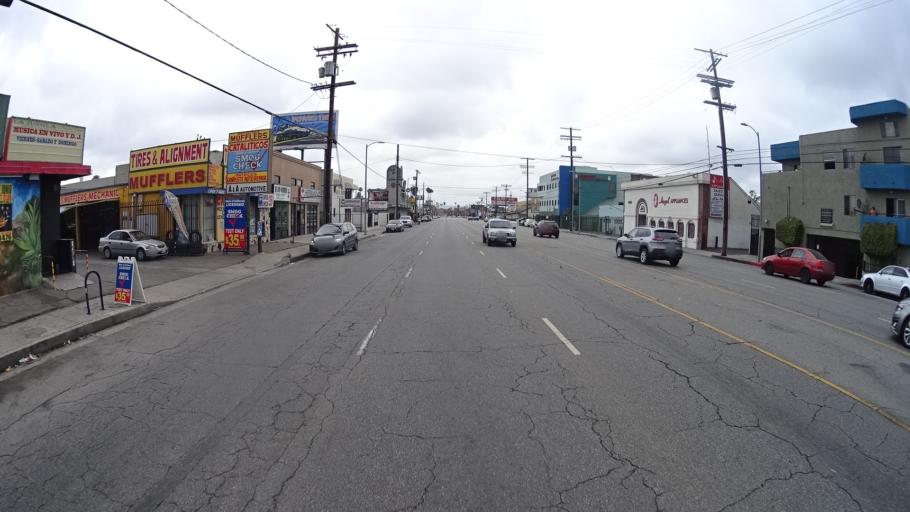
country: US
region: California
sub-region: Los Angeles County
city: Van Nuys
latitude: 34.2263
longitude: -118.4677
